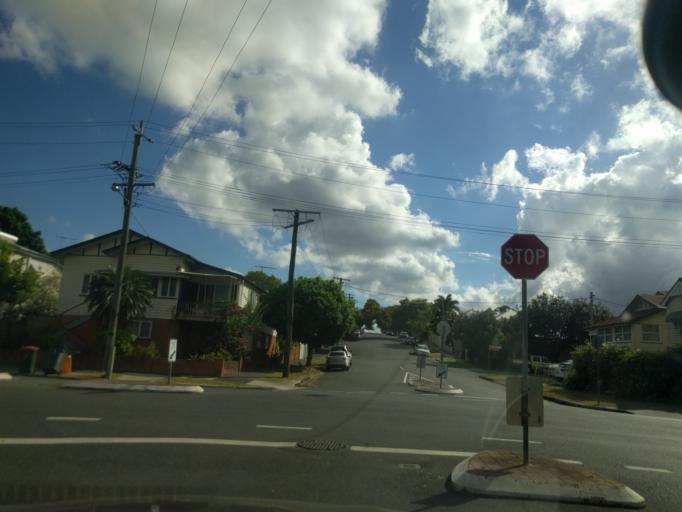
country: AU
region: Queensland
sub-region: Brisbane
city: Balmoral
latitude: -27.4630
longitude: 153.0481
